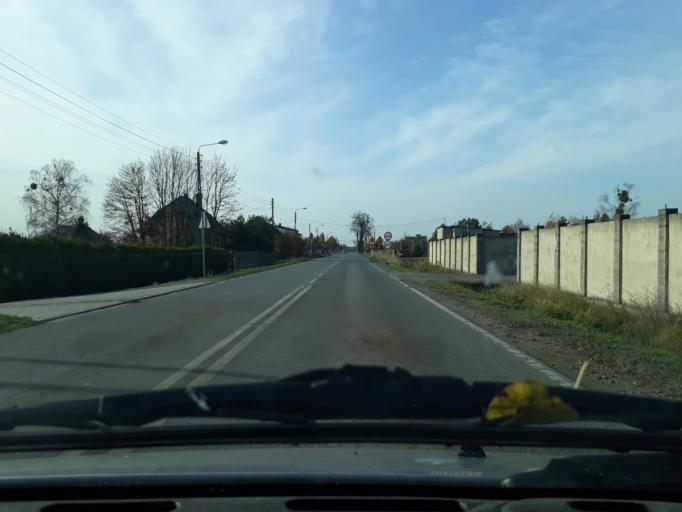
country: PL
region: Silesian Voivodeship
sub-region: Powiat lubliniecki
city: Psary
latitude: 50.5770
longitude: 19.0002
